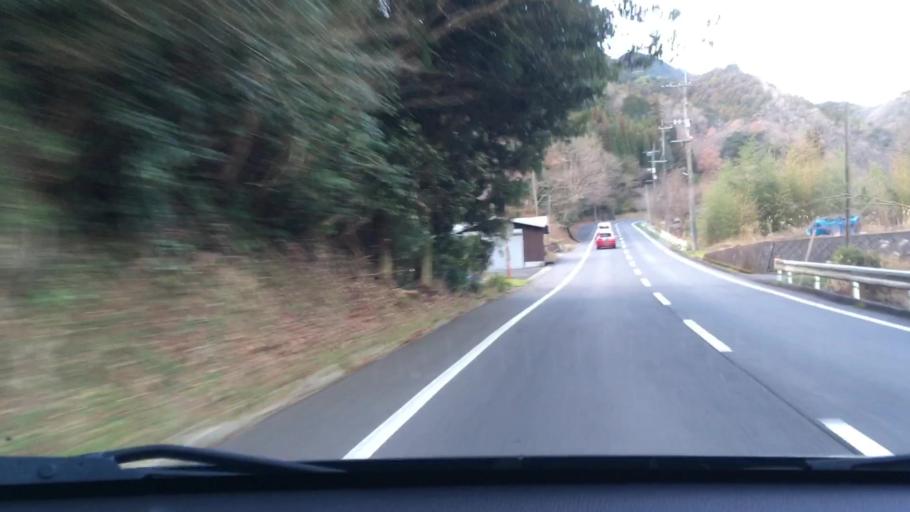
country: JP
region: Oita
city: Bungo-Takada-shi
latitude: 33.4692
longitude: 131.3863
